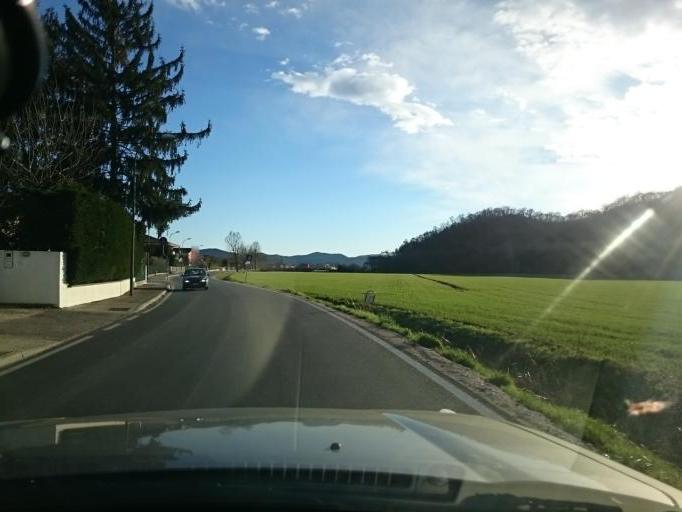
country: IT
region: Veneto
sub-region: Provincia di Padova
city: San Biagio
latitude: 45.3635
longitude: 11.7440
